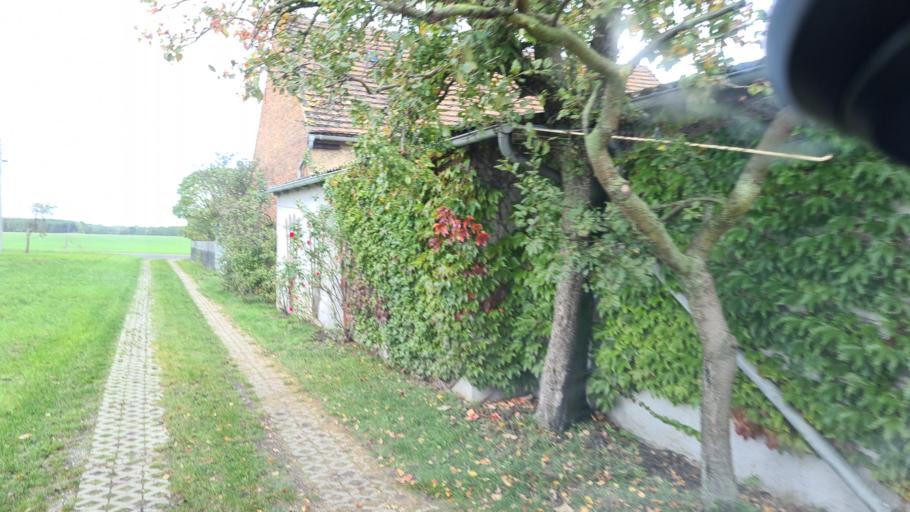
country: DE
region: Brandenburg
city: Sallgast
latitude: 51.6062
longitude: 13.8929
